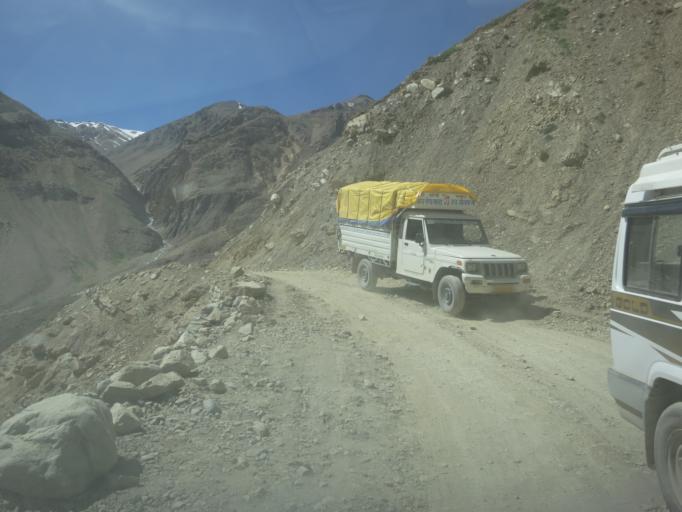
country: IN
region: Himachal Pradesh
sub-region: Kulu
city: Manali
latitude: 32.4303
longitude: 77.6755
